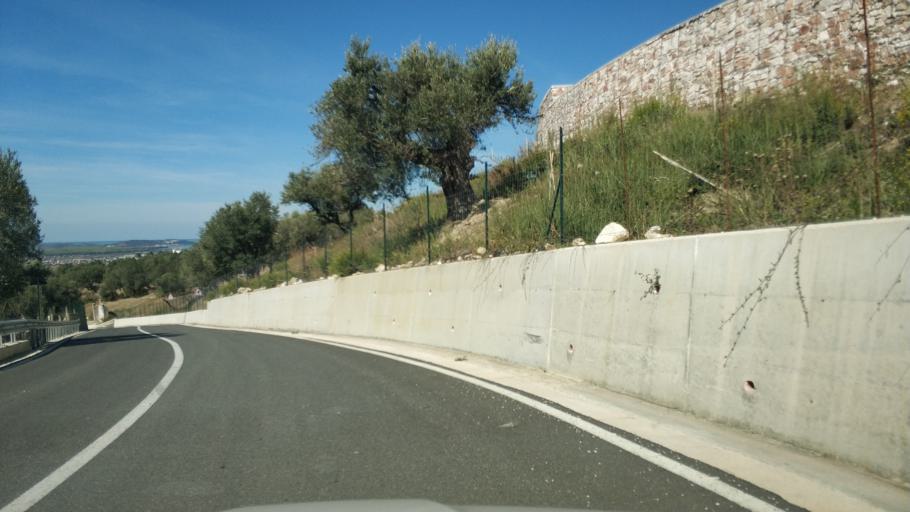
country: AL
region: Vlore
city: Vlore
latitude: 40.4570
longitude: 19.5106
